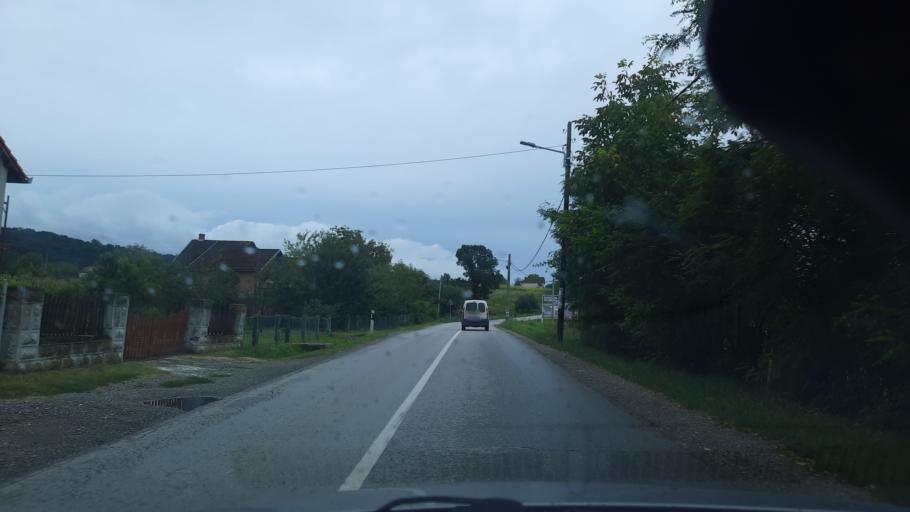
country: RS
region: Central Serbia
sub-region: Raski Okrug
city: Vrnjacka Banja
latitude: 43.7136
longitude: 20.8305
